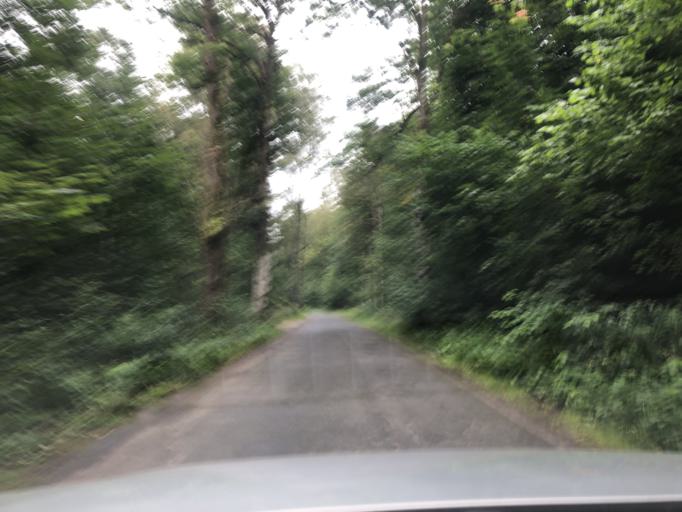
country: PL
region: Greater Poland Voivodeship
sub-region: Powiat pilski
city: Szydlowo
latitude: 53.2685
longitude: 16.6429
